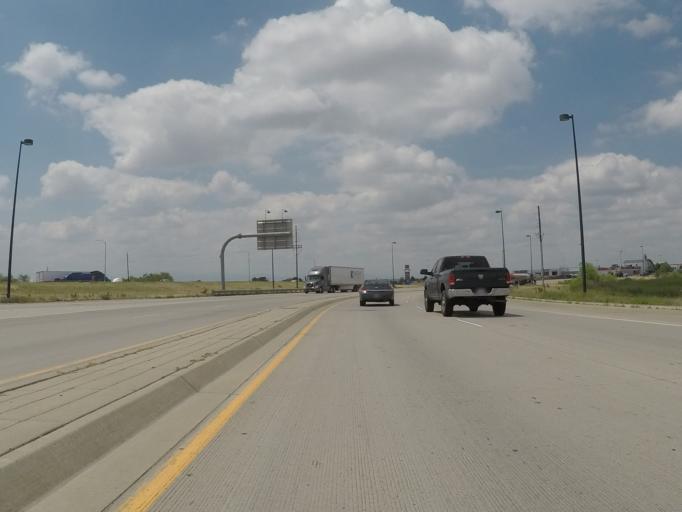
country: US
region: Colorado
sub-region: Adams County
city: Commerce City
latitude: 39.7872
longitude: -104.9019
